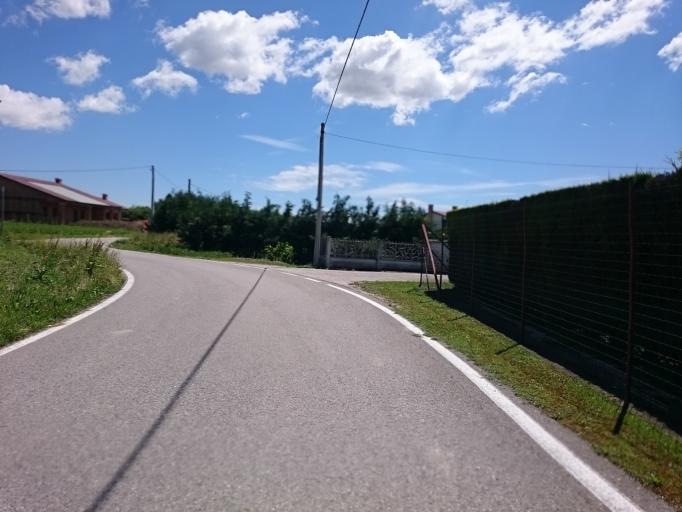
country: IT
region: Veneto
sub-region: Provincia di Padova
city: Polverara
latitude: 45.3095
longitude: 11.9690
